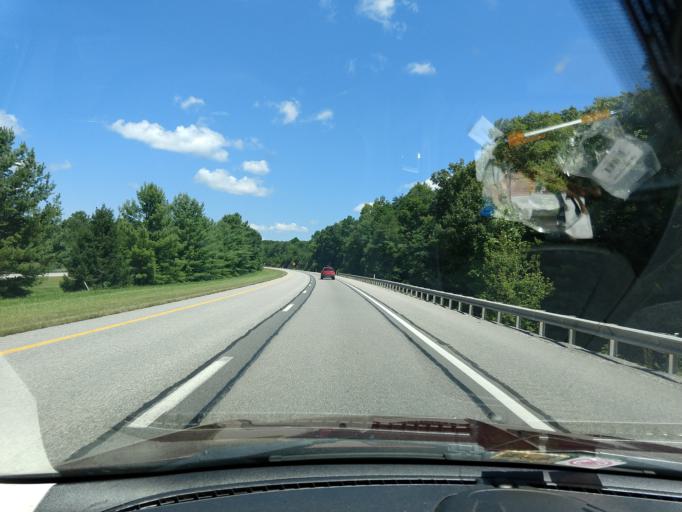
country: US
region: West Virginia
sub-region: Fayette County
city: Ansted
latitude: 38.1004
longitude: -81.0242
